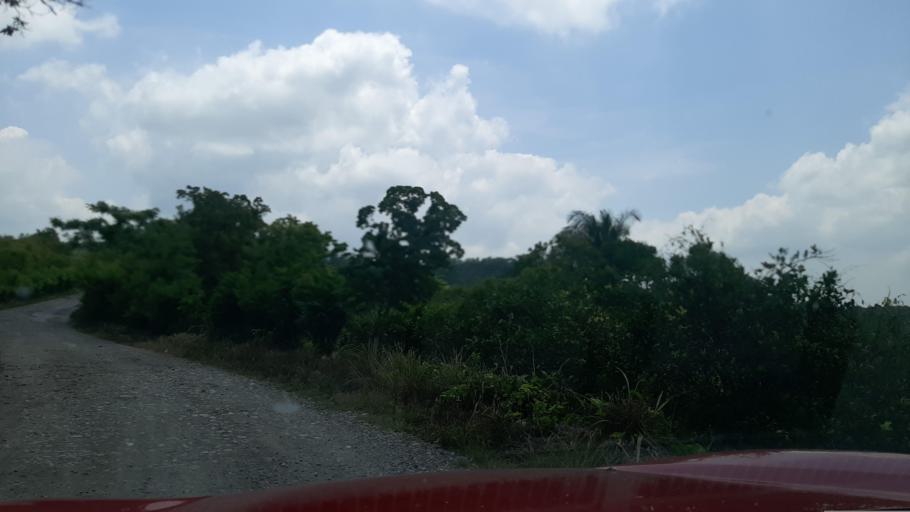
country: MX
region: Veracruz
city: Agua Dulce
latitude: 20.4100
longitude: -97.2836
